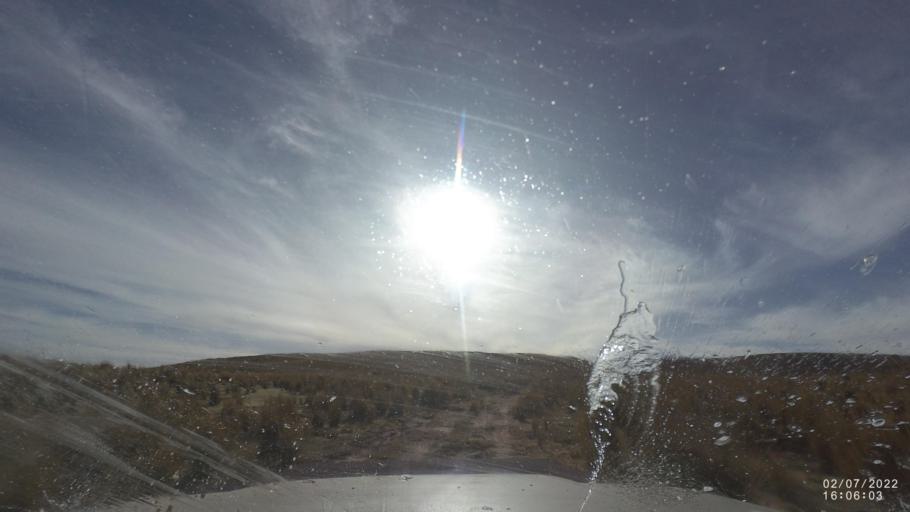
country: BO
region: Cochabamba
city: Irpa Irpa
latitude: -17.9119
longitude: -66.4429
